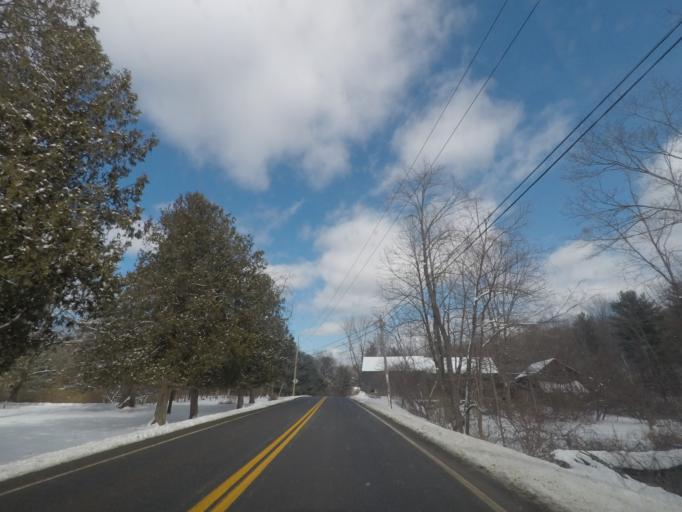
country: US
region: New York
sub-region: Rensselaer County
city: Nassau
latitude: 42.4646
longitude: -73.5380
